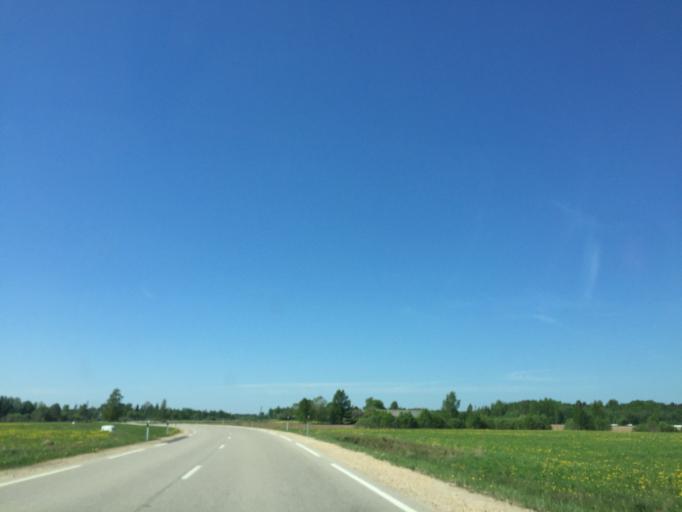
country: LV
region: Malpils
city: Malpils
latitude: 56.8964
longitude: 24.8982
